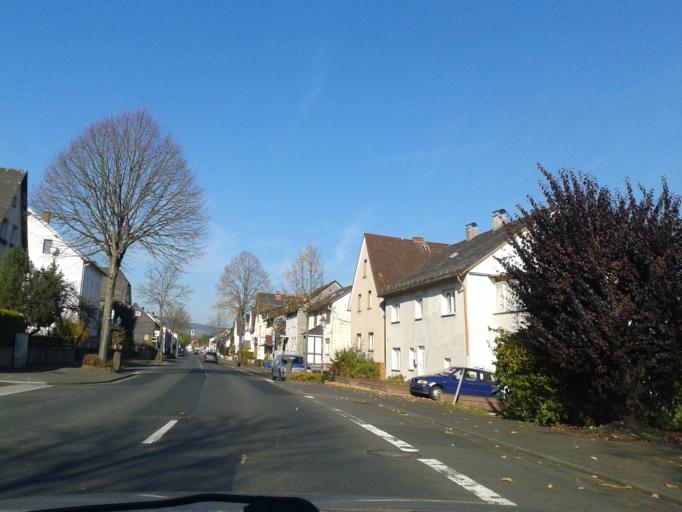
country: DE
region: Hesse
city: Dillenburg
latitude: 50.8094
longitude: 8.3383
